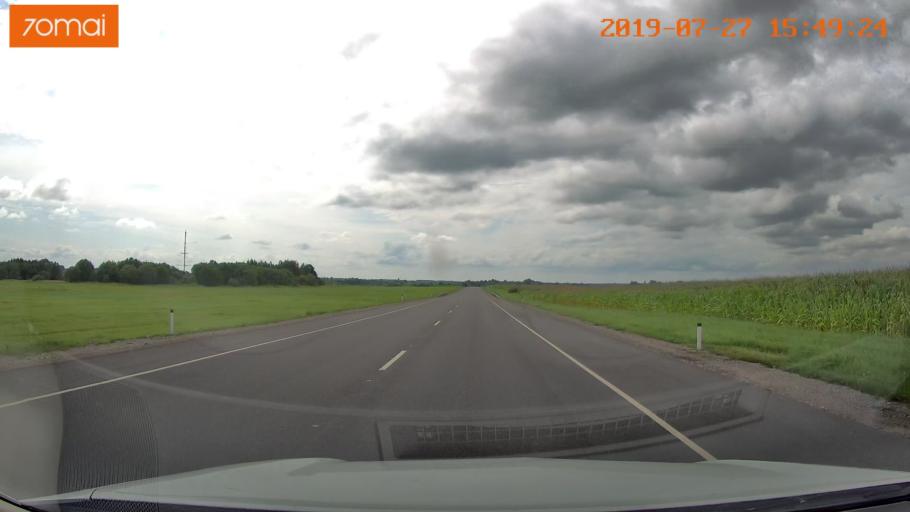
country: RU
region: Kaliningrad
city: Gusev
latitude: 54.6016
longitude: 22.0350
